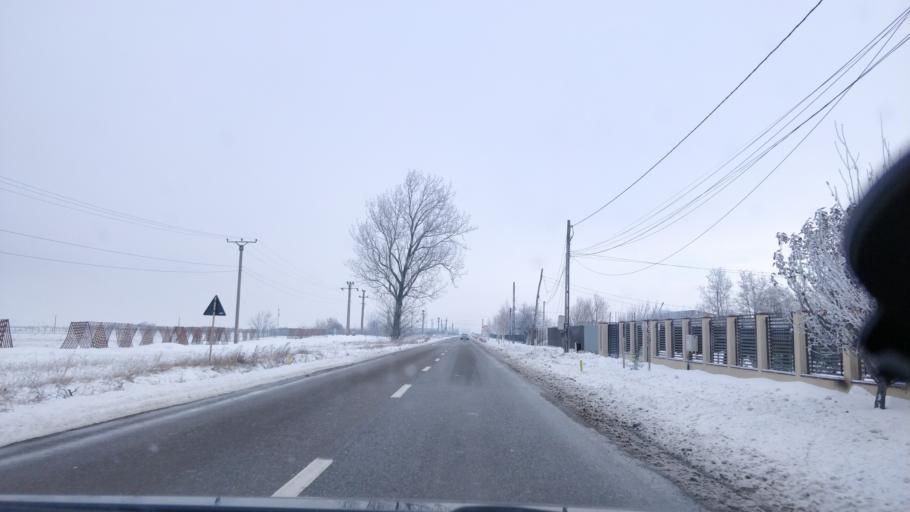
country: RO
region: Vrancea
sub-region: Comuna Vrancioaia
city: Focsani
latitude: 45.6979
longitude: 27.2097
